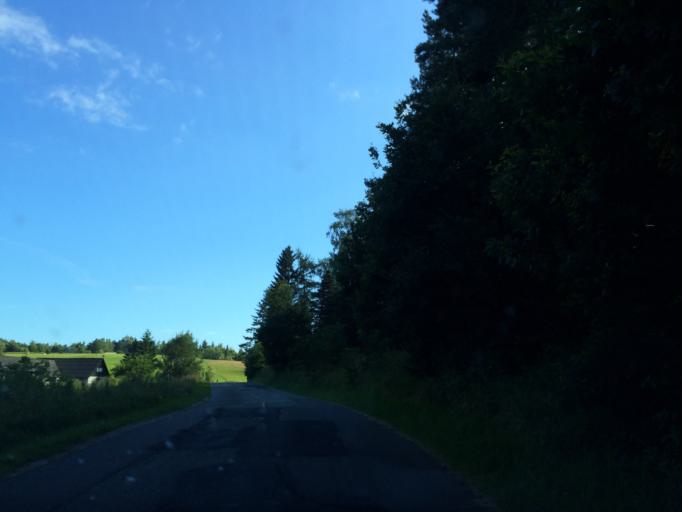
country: DK
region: Central Jutland
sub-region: Syddjurs Kommune
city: Ebeltoft
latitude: 56.2518
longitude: 10.6241
